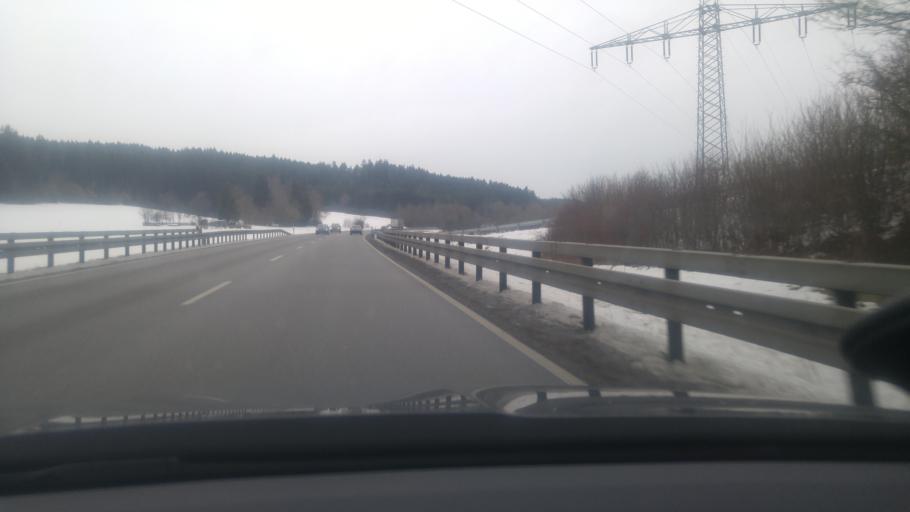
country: DE
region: Baden-Wuerttemberg
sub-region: Freiburg Region
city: Dauchingen
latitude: 48.0566
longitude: 8.5659
